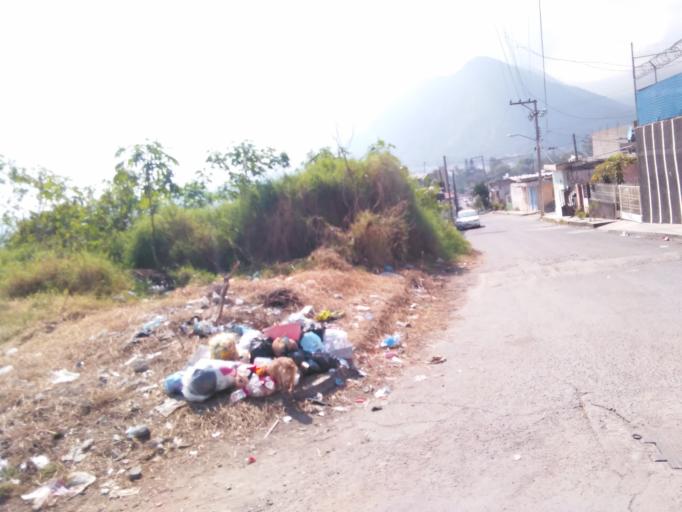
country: MX
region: Nayarit
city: Tepic
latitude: 21.5288
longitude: -104.9186
